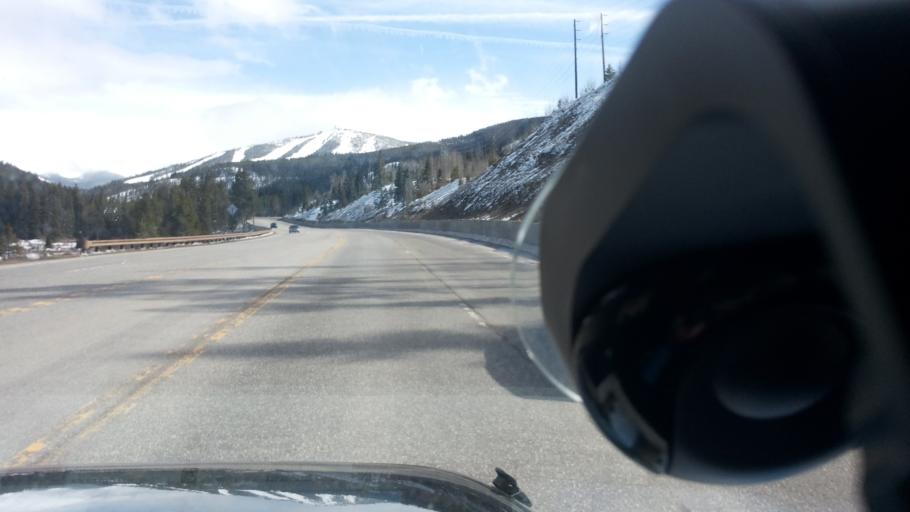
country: US
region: Colorado
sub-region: Grand County
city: Fraser
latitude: 39.9120
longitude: -105.7821
